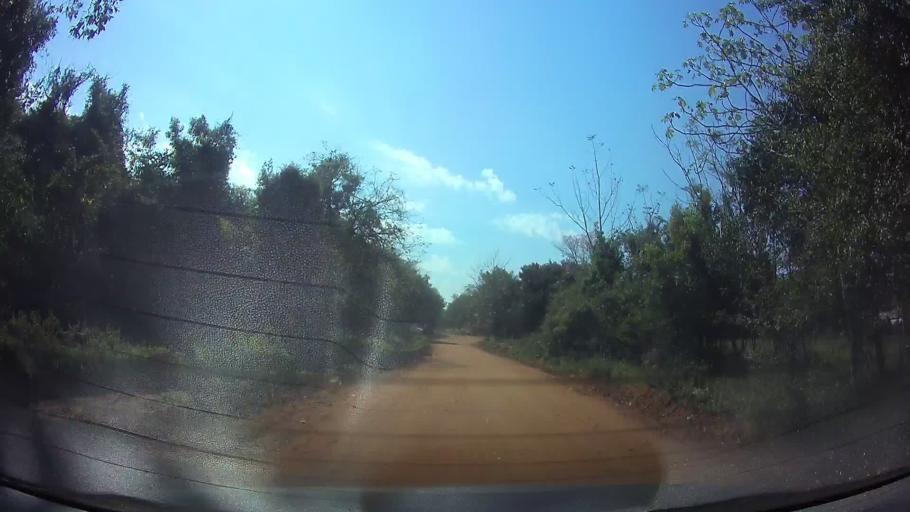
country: PY
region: Central
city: Limpio
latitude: -25.2260
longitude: -57.4400
